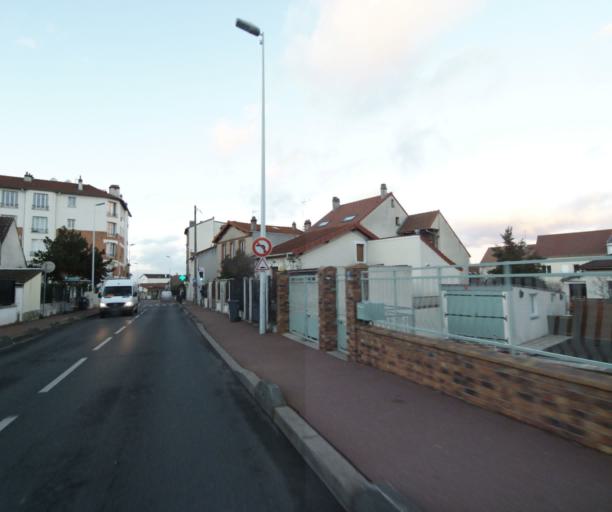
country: FR
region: Ile-de-France
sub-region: Departement des Hauts-de-Seine
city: Nanterre
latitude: 48.8820
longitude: 2.2178
